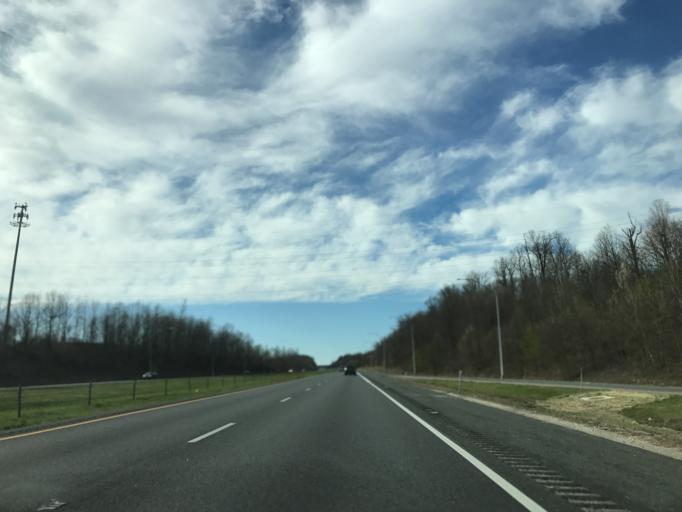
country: US
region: Maryland
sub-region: Baltimore County
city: Owings Mills
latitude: 39.4164
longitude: -76.7960
